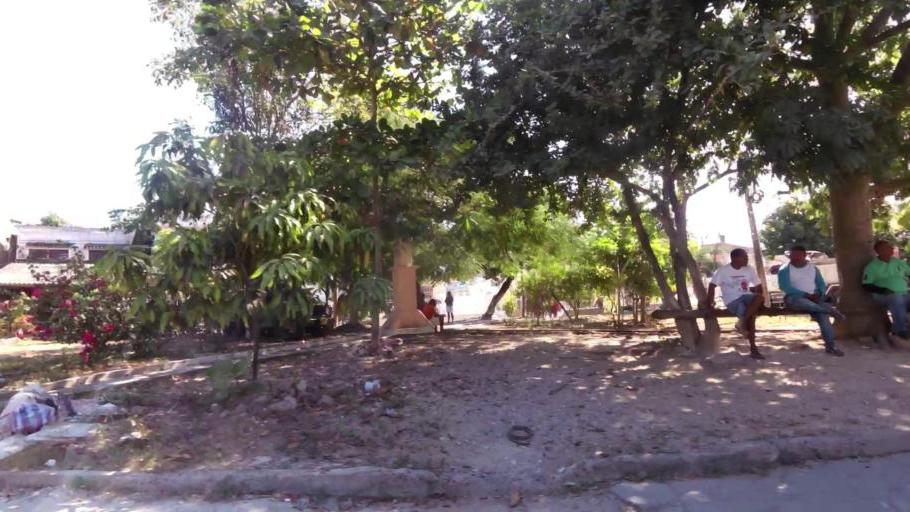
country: CO
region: Bolivar
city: Cartagena
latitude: 10.3932
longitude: -75.5073
